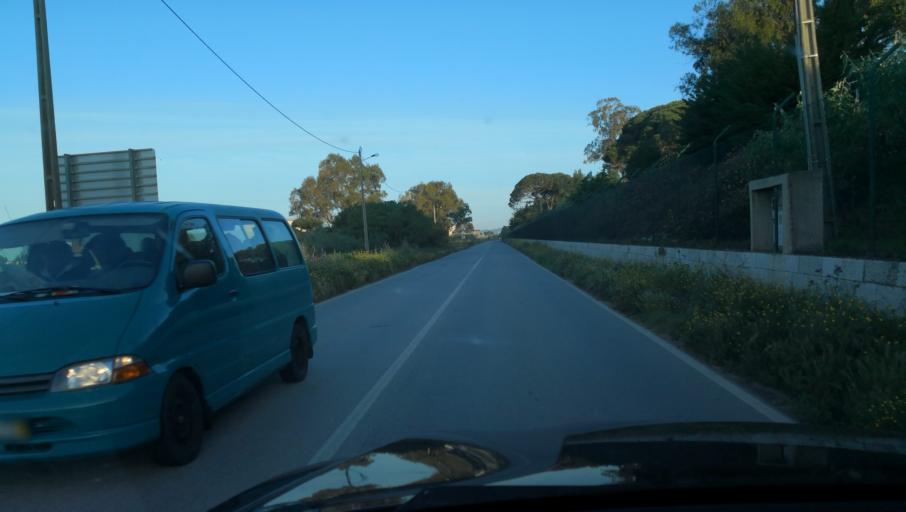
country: PT
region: Setubal
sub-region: Setubal
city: Setubal
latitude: 38.4888
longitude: -8.8101
